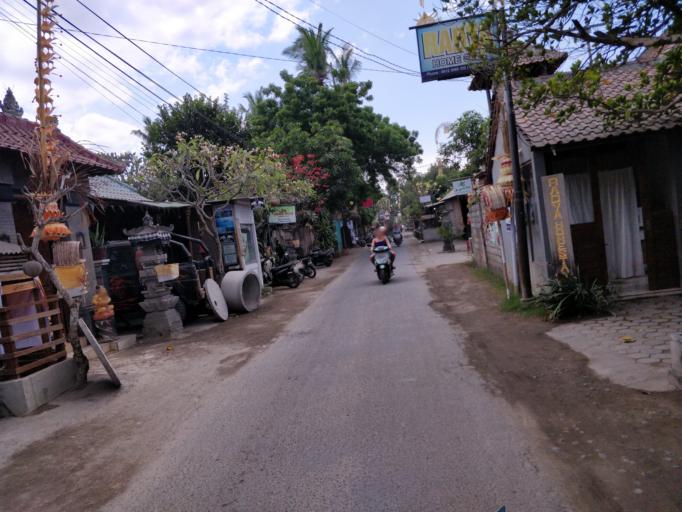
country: ID
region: Bali
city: Jungutbatu Kaja Dua
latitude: -8.6741
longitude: 115.4490
